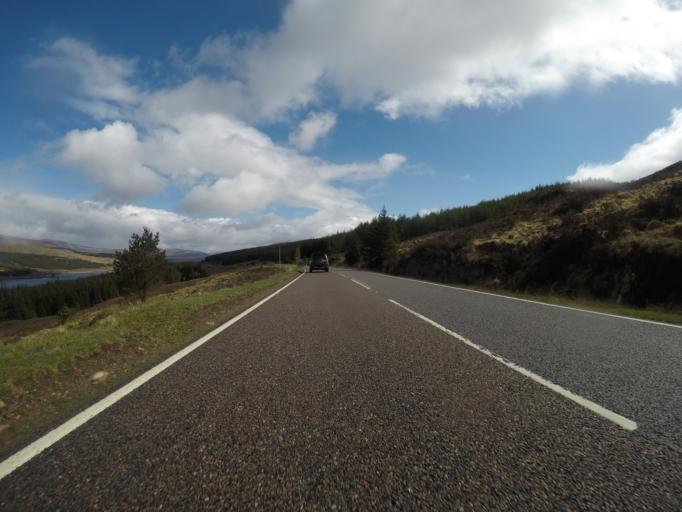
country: GB
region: Scotland
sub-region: Highland
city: Spean Bridge
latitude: 57.1023
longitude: -4.9899
